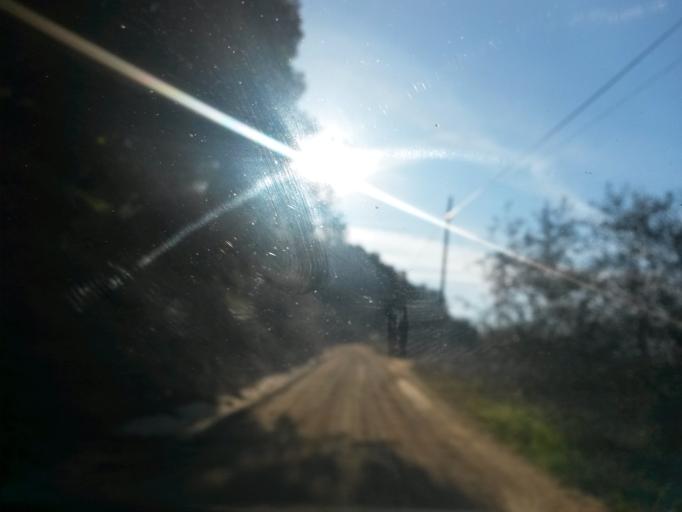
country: ES
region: Catalonia
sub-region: Provincia de Girona
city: la Cellera de Ter
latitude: 41.9721
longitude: 2.6295
